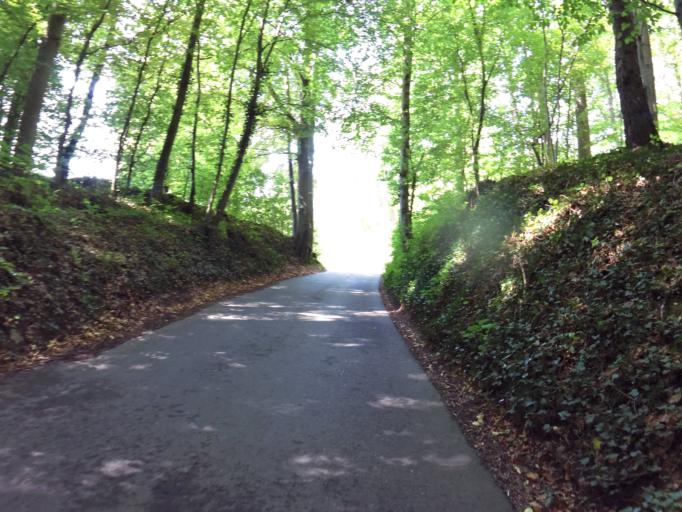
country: DE
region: Baden-Wuerttemberg
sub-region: Karlsruhe Region
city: Eschelbronn
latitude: 49.3297
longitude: 8.8501
